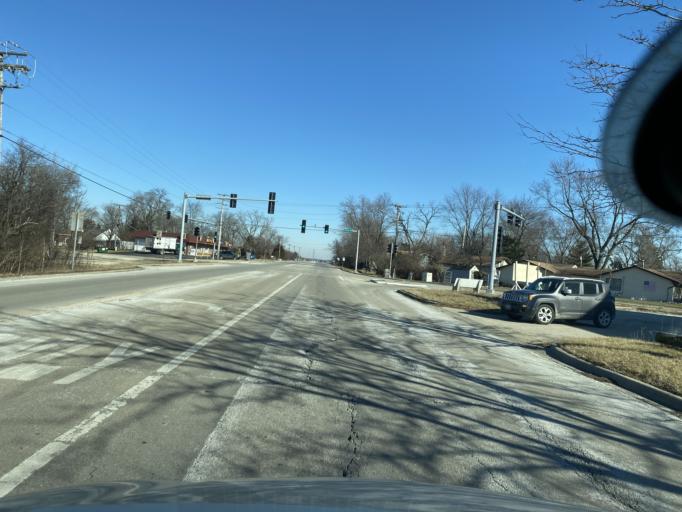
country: US
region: Illinois
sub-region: Will County
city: Lockport
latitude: 41.6224
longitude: -88.0276
